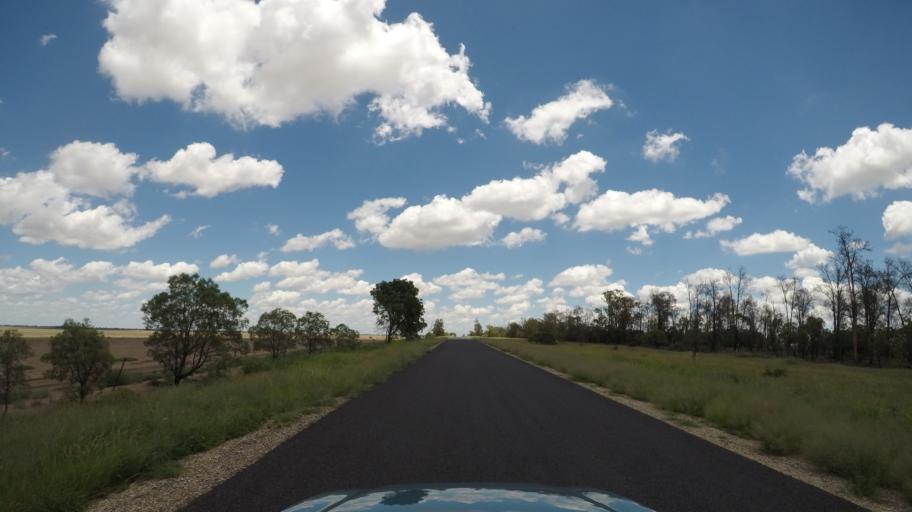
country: AU
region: Queensland
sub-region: Goondiwindi
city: Goondiwindi
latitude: -28.1631
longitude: 150.1539
